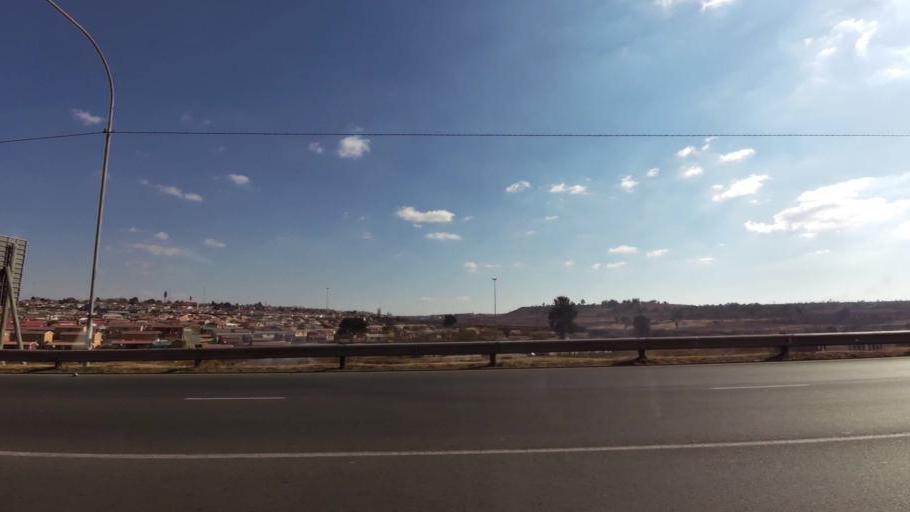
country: ZA
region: Gauteng
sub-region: City of Johannesburg Metropolitan Municipality
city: Soweto
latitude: -26.2257
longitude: 27.9273
